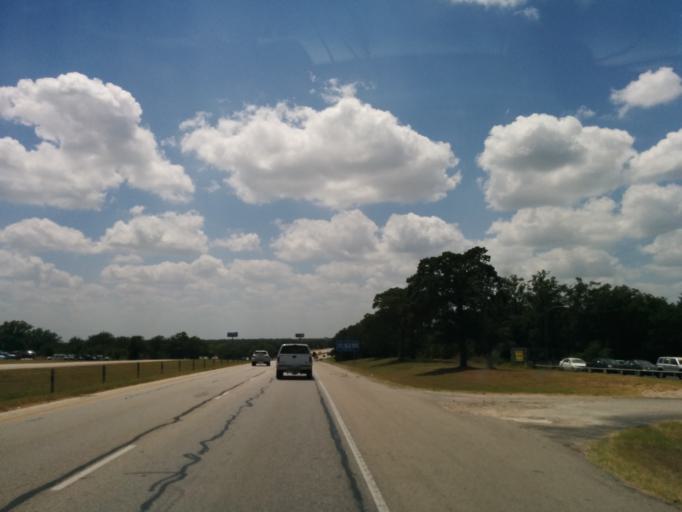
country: US
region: Texas
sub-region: Bastrop County
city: Wyldwood
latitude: 30.1108
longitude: -97.4044
